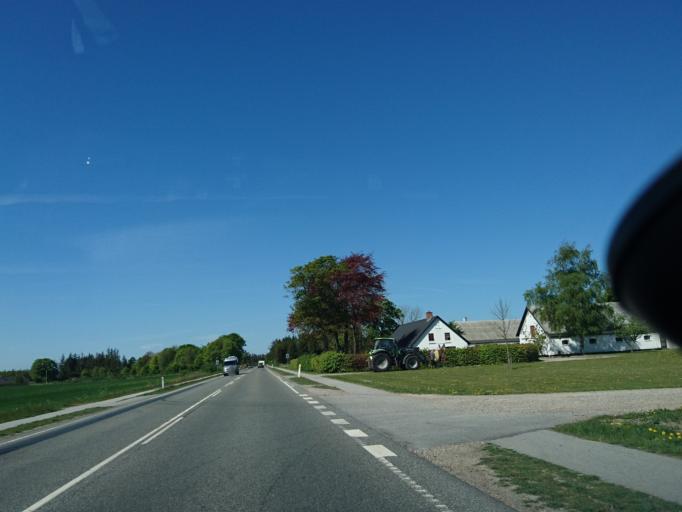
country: DK
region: North Denmark
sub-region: Hjorring Kommune
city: Tars
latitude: 57.4552
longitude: 10.1218
